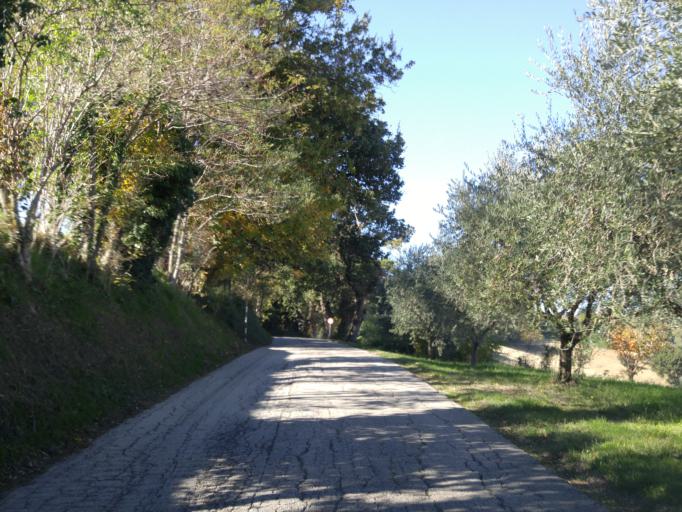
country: IT
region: The Marches
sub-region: Provincia di Pesaro e Urbino
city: Serrungarina
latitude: 43.7439
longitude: 12.8707
